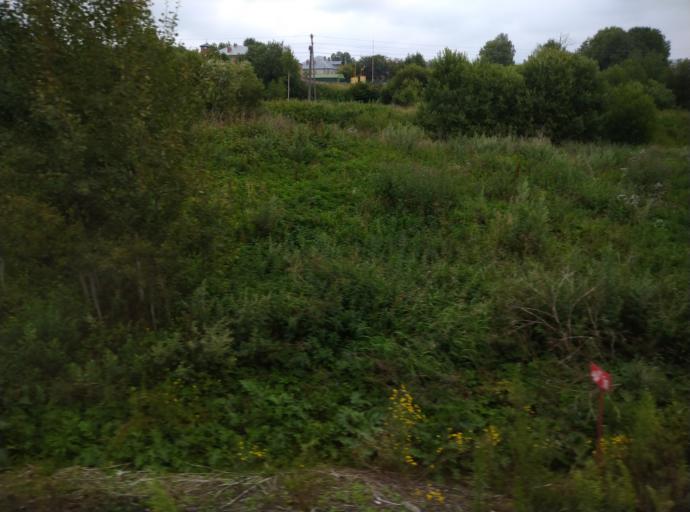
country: RU
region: Kostroma
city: Kosmynino
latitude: 57.5831
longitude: 40.7534
